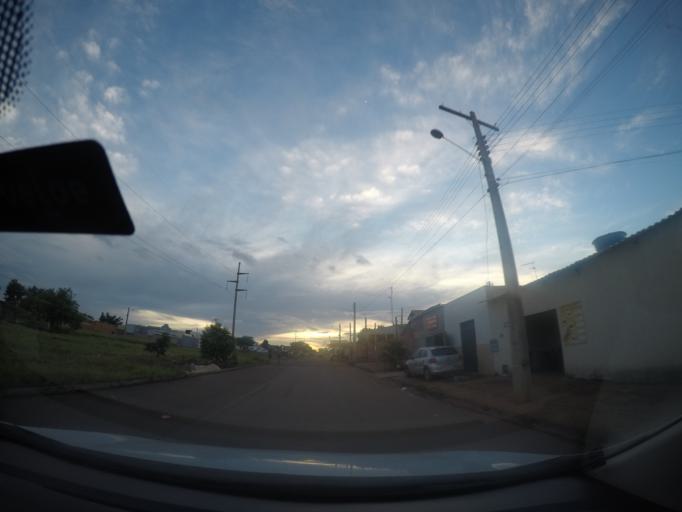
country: BR
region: Goias
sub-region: Goianira
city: Goianira
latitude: -16.5714
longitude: -49.3837
